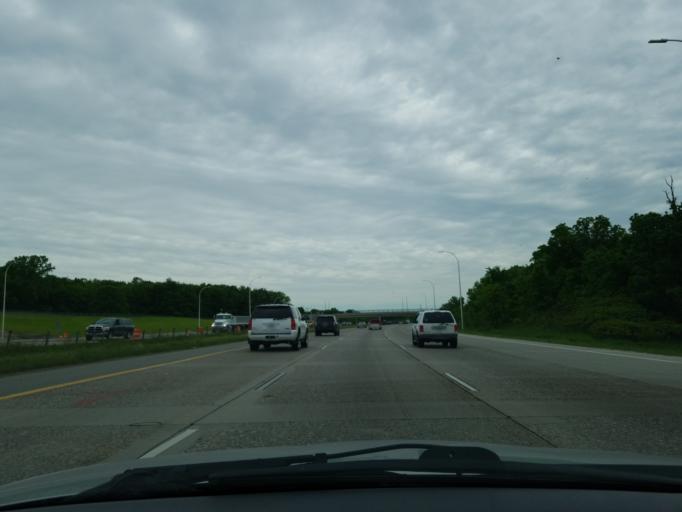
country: US
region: Minnesota
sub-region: Hennepin County
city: Corcoran
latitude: 45.1414
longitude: -93.4969
